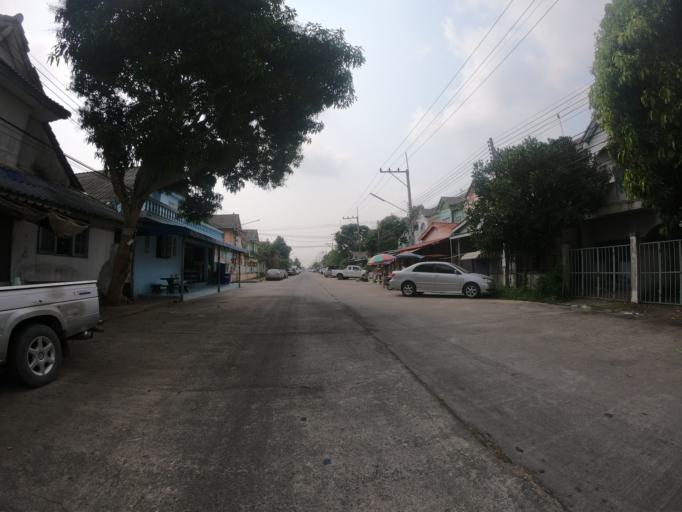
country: TH
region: Pathum Thani
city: Nong Suea
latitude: 14.0751
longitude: 100.8585
